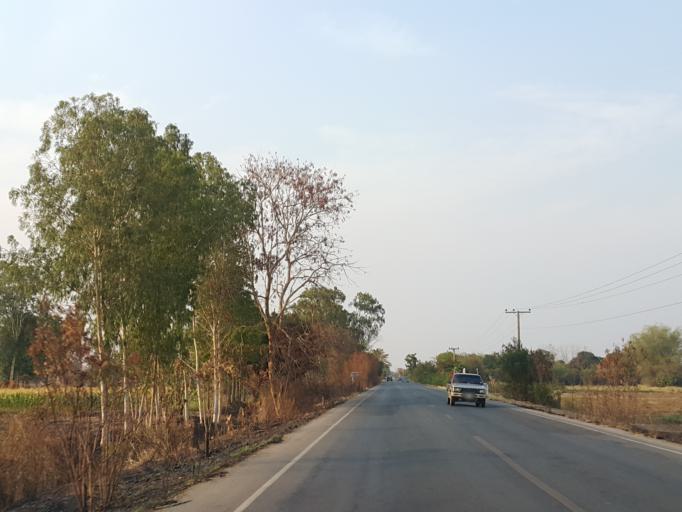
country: TH
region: Sukhothai
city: Si Samrong
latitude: 17.2129
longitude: 99.9490
